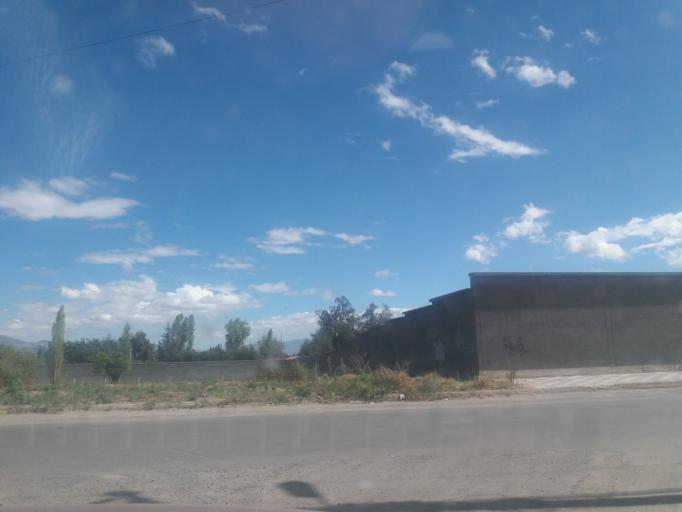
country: EC
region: Pichincha
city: Quito
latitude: -0.1702
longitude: -78.3399
